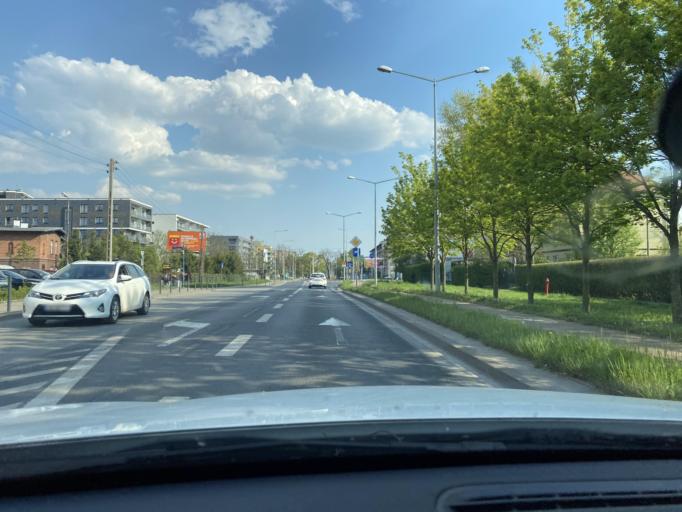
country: PL
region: Lower Silesian Voivodeship
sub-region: Powiat wroclawski
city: Wroclaw
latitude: 51.1427
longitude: 17.0254
